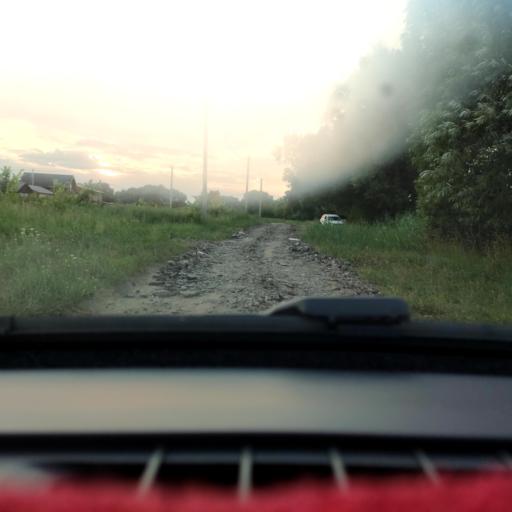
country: RU
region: Voronezj
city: Novaya Usman'
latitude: 51.6270
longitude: 39.3827
